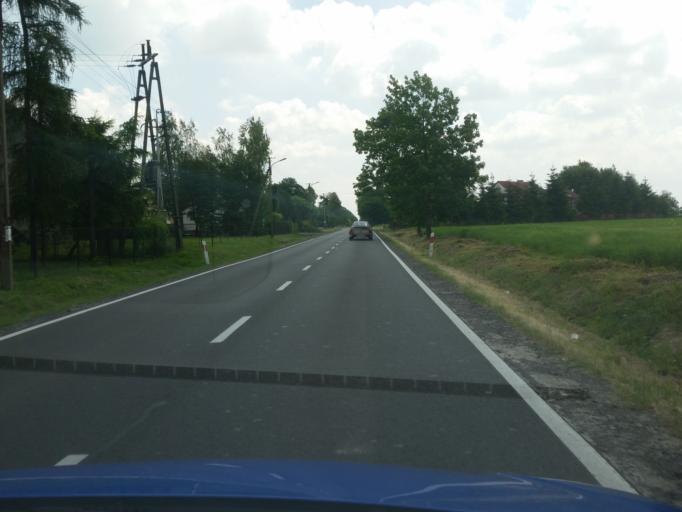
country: PL
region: Lesser Poland Voivodeship
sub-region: Powiat miechowski
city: Miechow
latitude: 50.3544
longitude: 20.1018
